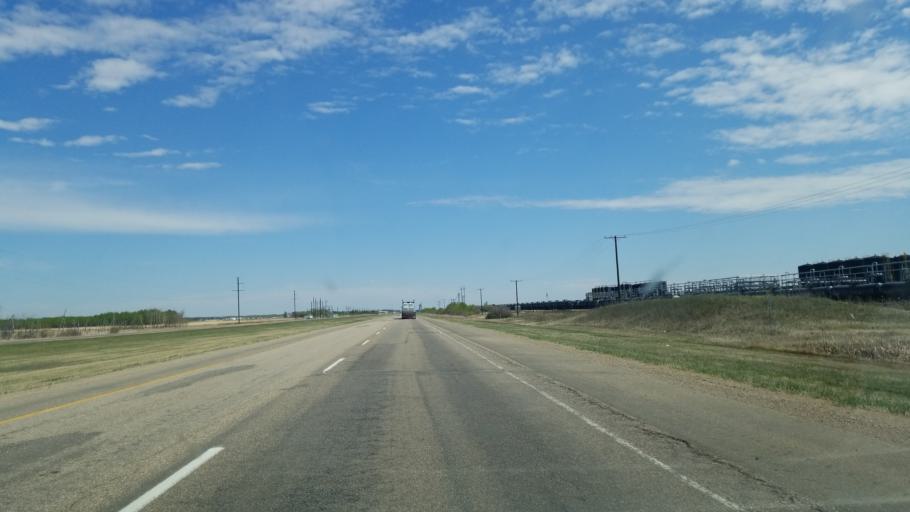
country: CA
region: Saskatchewan
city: Lloydminster
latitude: 53.1420
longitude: -109.6602
